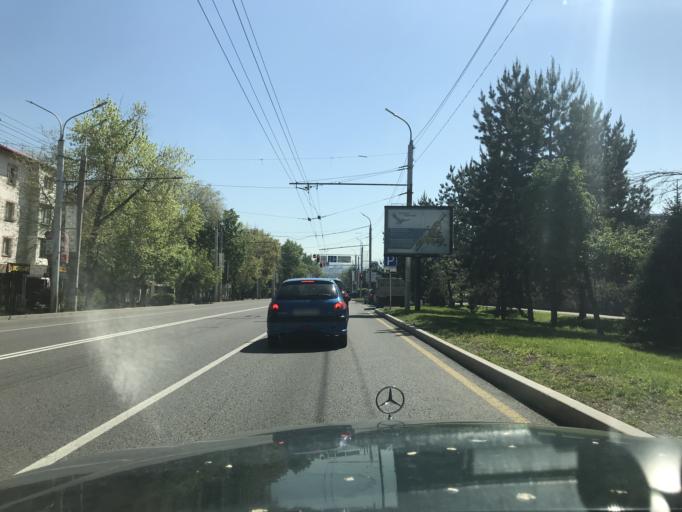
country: KZ
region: Almaty Qalasy
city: Almaty
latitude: 43.2260
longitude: 76.9085
